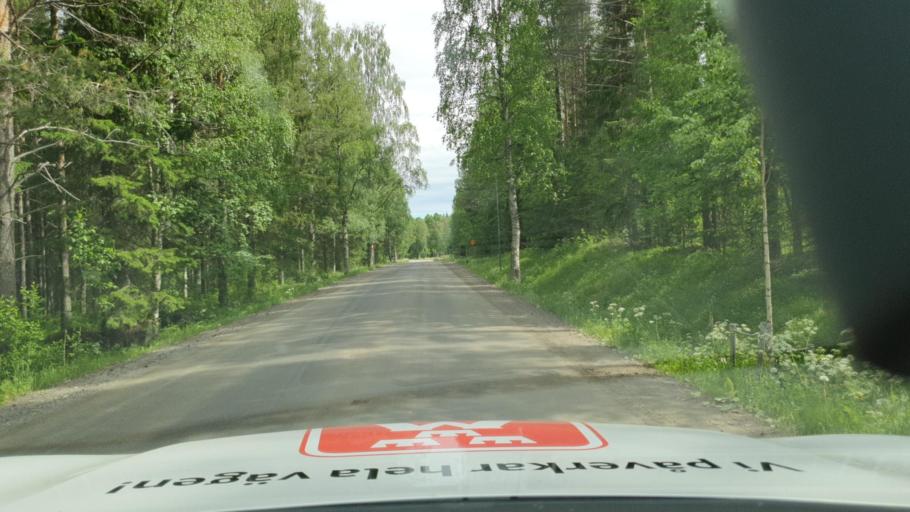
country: SE
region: Vaesterbotten
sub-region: Skelleftea Kommun
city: Burtraesk
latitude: 64.3484
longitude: 20.4908
